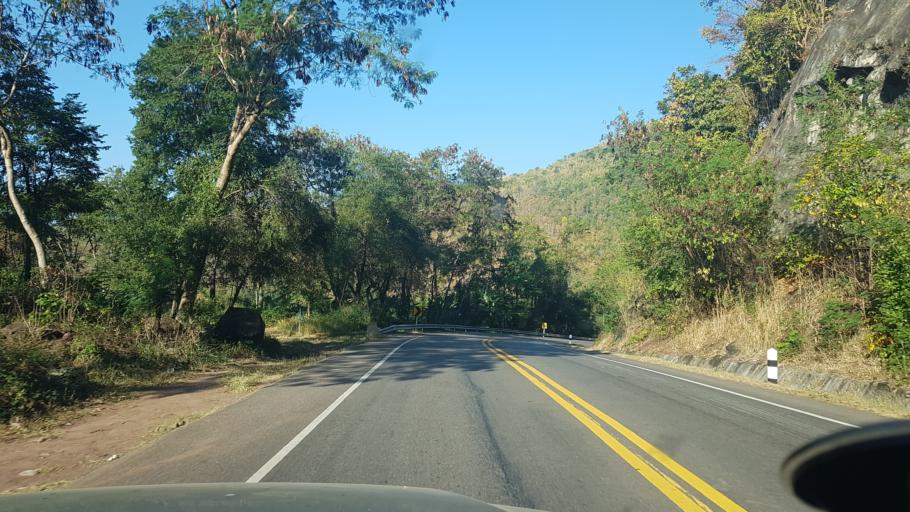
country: TH
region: Phetchabun
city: Lom Sak
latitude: 16.7462
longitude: 101.3993
